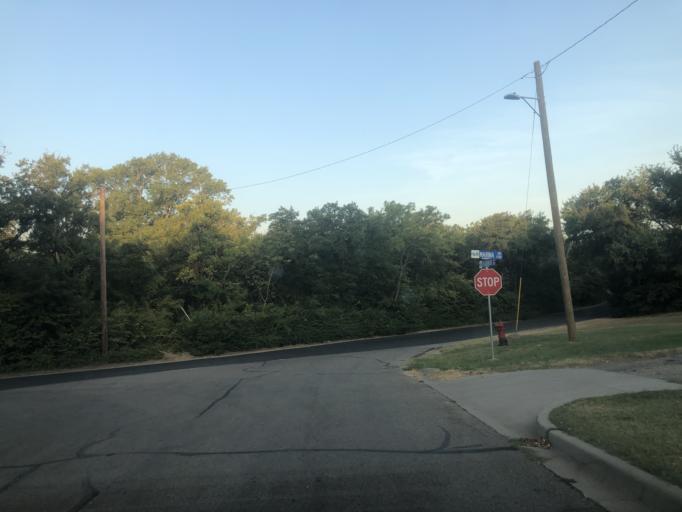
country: US
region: Texas
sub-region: Tarrant County
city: Lake Worth
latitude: 32.8096
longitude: -97.4461
